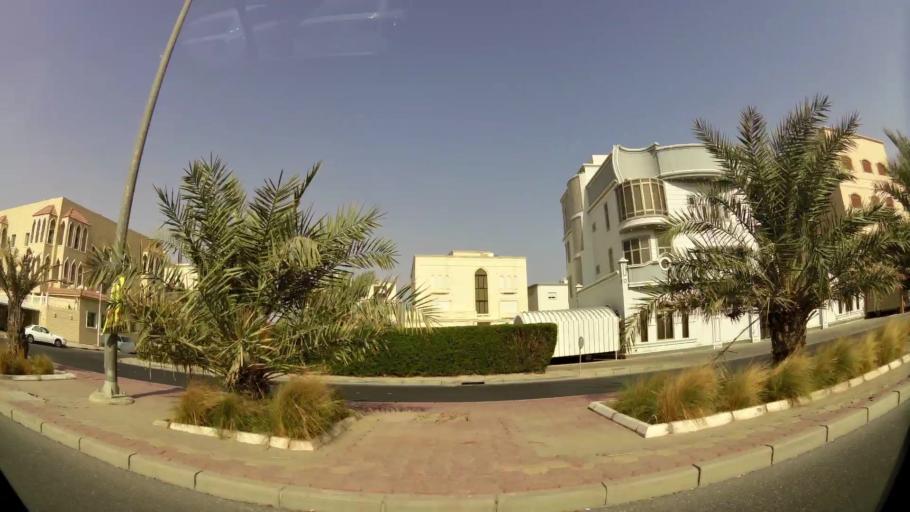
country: KW
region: Muhafazat al Jahra'
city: Al Jahra'
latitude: 29.3563
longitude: 47.6758
